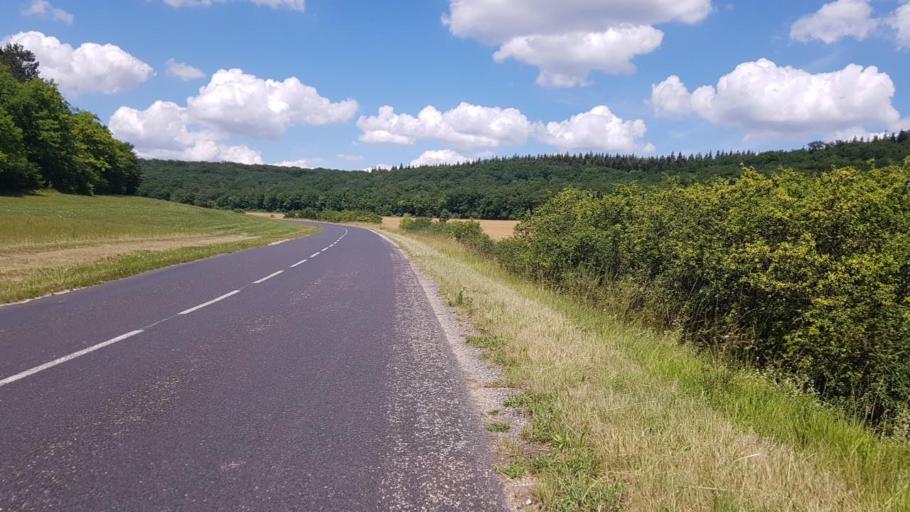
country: FR
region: Lorraine
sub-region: Departement de la Meuse
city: Vacon
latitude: 48.6713
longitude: 5.5975
